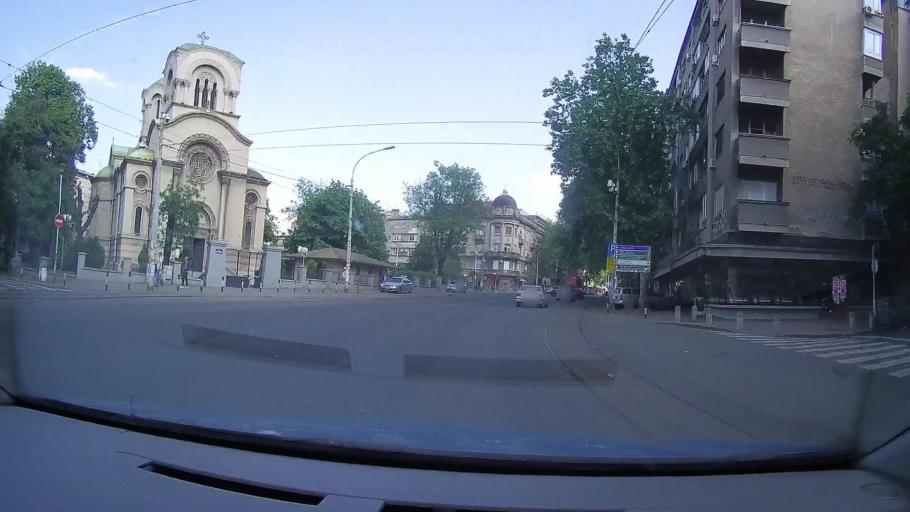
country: RS
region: Central Serbia
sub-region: Belgrade
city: Stari Grad
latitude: 44.8205
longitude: 20.4654
